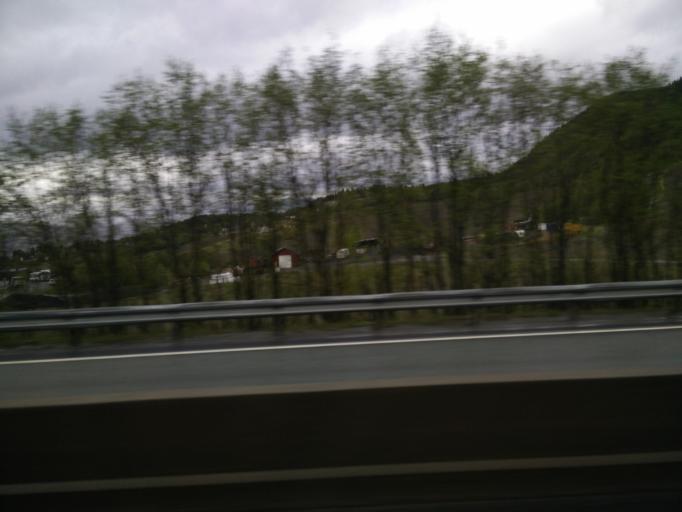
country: NO
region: Sor-Trondelag
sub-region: Malvik
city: Malvik
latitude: 63.4241
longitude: 10.5762
